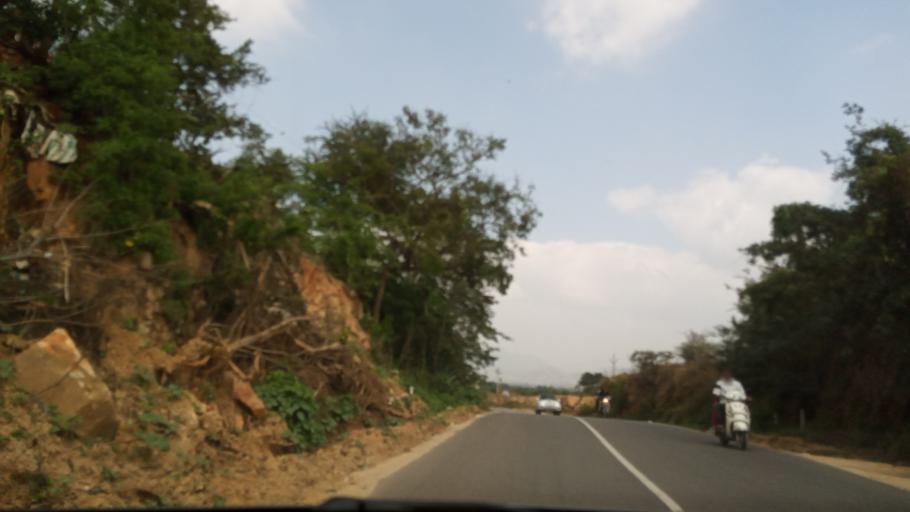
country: IN
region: Andhra Pradesh
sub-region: Chittoor
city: Madanapalle
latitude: 13.5856
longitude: 78.5234
